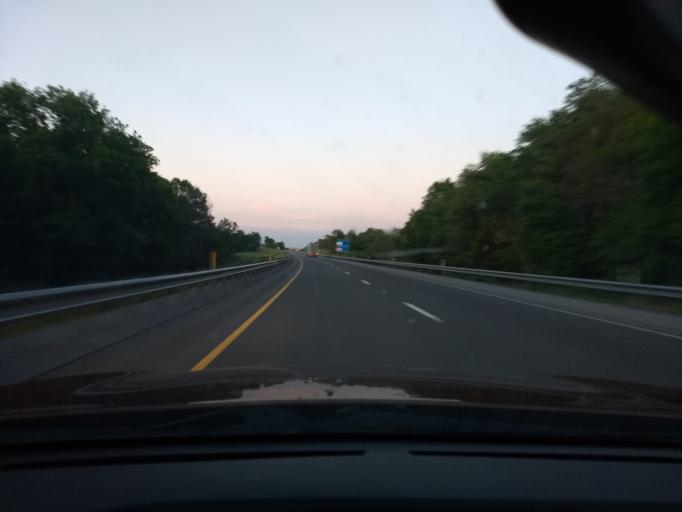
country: US
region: Pennsylvania
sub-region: Clinton County
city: Castanea
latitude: 41.0472
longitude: -77.3225
